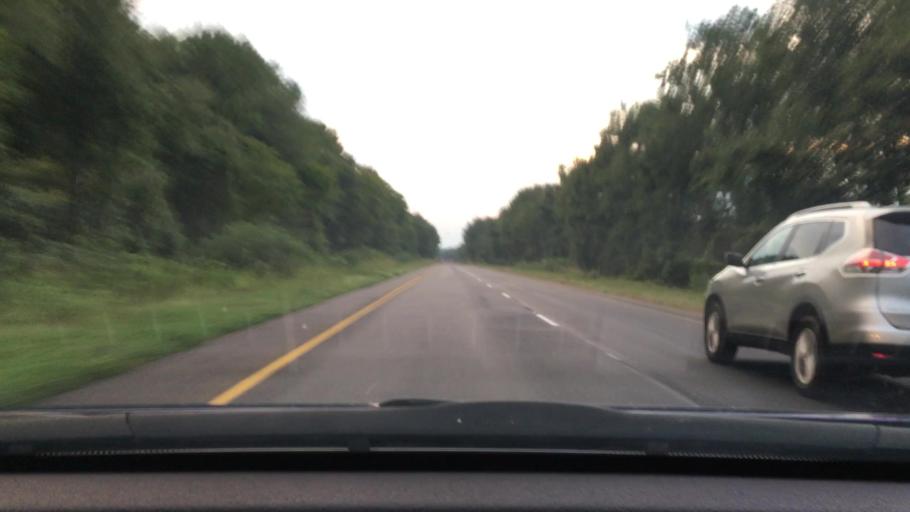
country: US
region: South Carolina
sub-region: Sumter County
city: Stateburg
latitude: 33.9502
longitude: -80.6041
